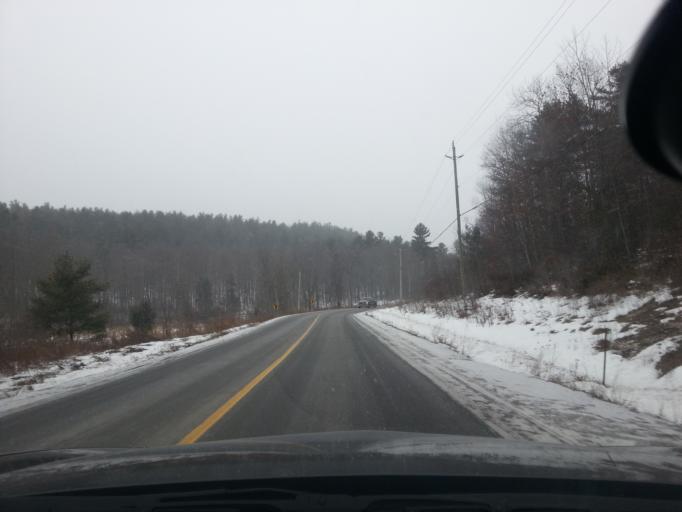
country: CA
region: Ontario
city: Arnprior
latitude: 45.3190
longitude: -76.3164
